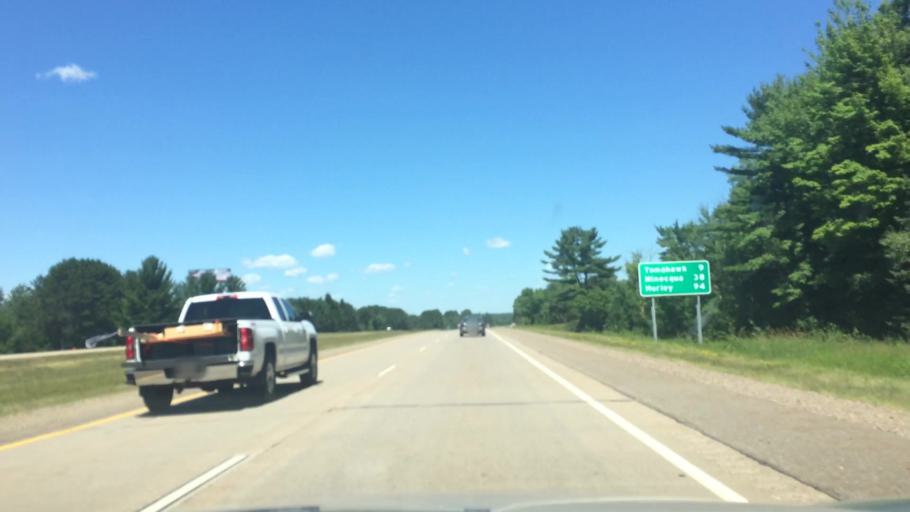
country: US
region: Wisconsin
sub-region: Lincoln County
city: Tomahawk
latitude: 45.3547
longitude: -89.6663
